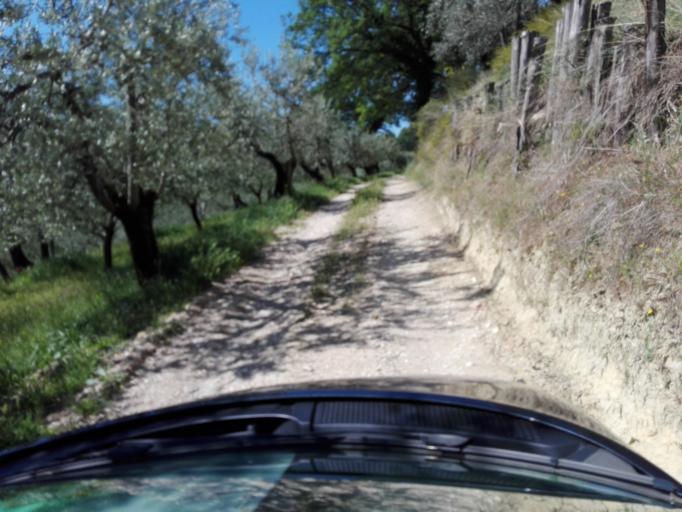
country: IT
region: Umbria
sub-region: Provincia di Perugia
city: Foligno
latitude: 42.9766
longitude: 12.7426
